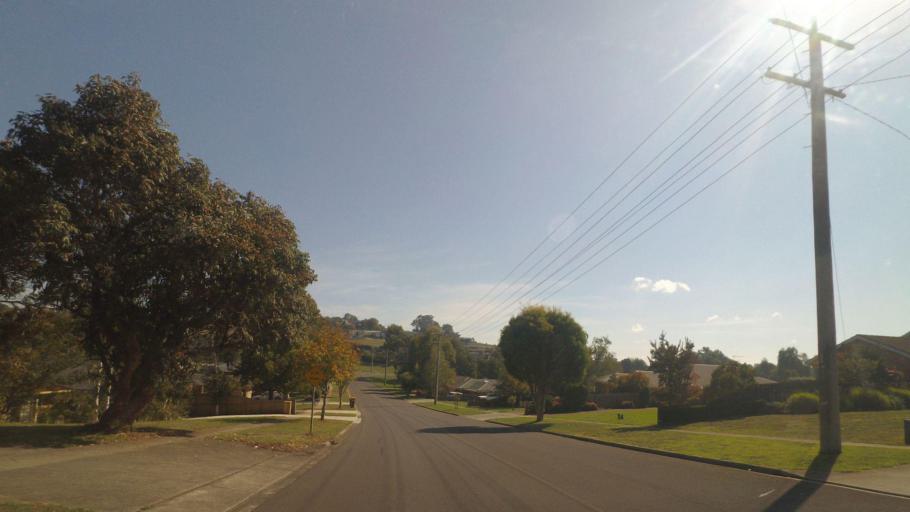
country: AU
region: Victoria
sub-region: Baw Baw
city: Warragul
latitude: -38.1436
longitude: 145.9458
